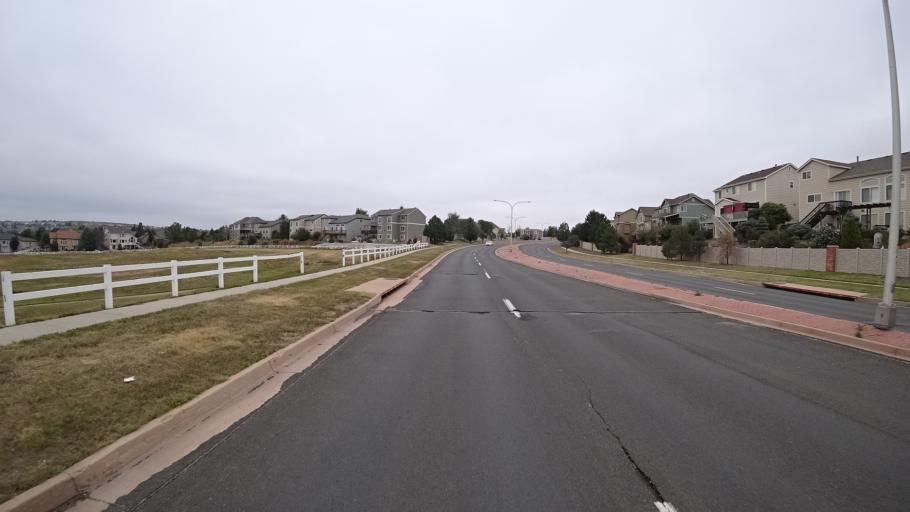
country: US
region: Colorado
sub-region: El Paso County
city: Cimarron Hills
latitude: 38.8936
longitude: -104.7022
